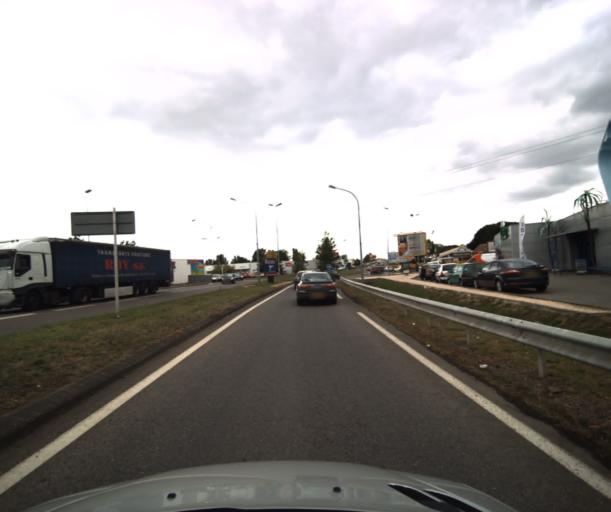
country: FR
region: Midi-Pyrenees
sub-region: Departement de la Haute-Garonne
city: Portet-sur-Garonne
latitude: 43.5329
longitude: 1.3993
